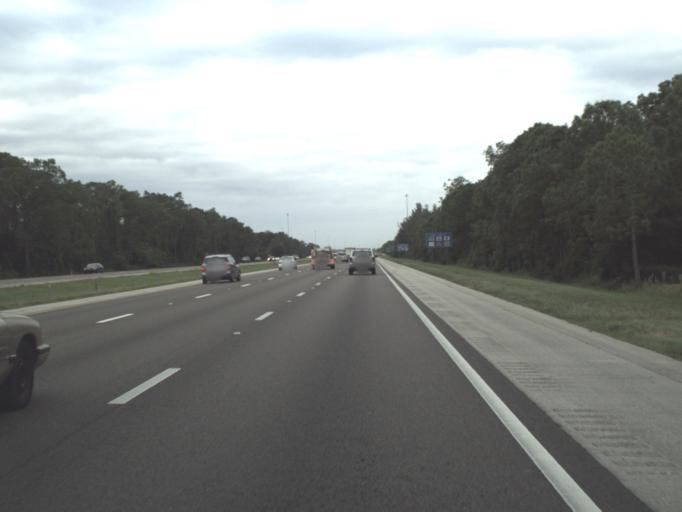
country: US
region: Florida
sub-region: Collier County
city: Vineyards
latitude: 26.2251
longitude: -81.7366
